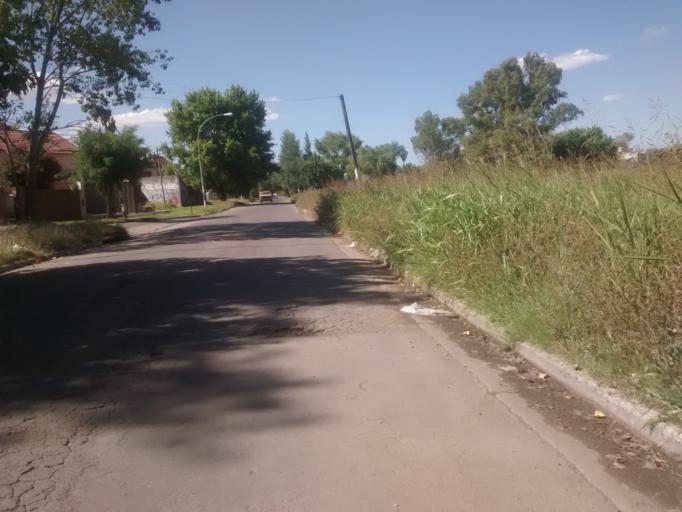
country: AR
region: Buenos Aires
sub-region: Partido de La Plata
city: La Plata
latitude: -34.9318
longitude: -57.9005
